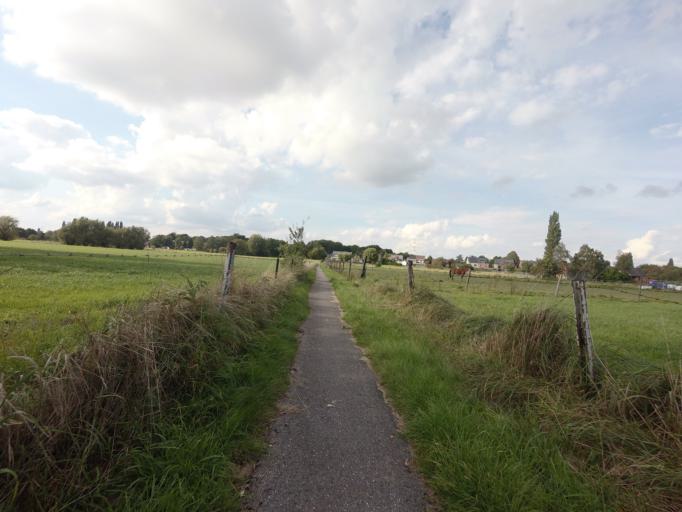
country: BE
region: Flanders
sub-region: Provincie Antwerpen
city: Boom
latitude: 51.1080
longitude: 4.3784
